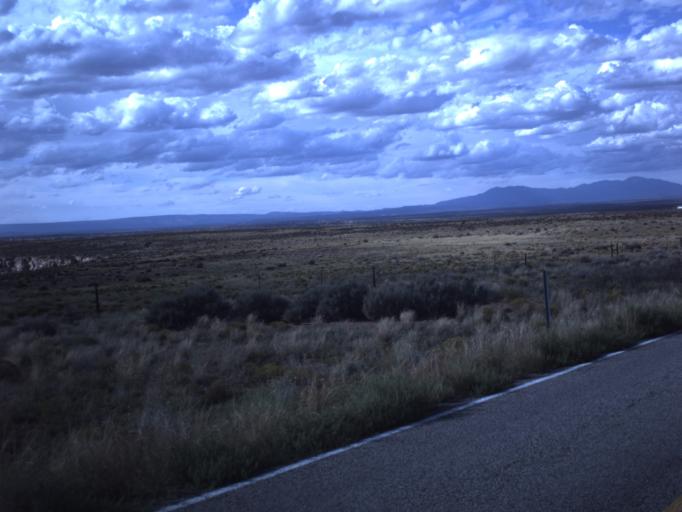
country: US
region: Utah
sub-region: San Juan County
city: Blanding
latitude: 37.3417
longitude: -109.3490
